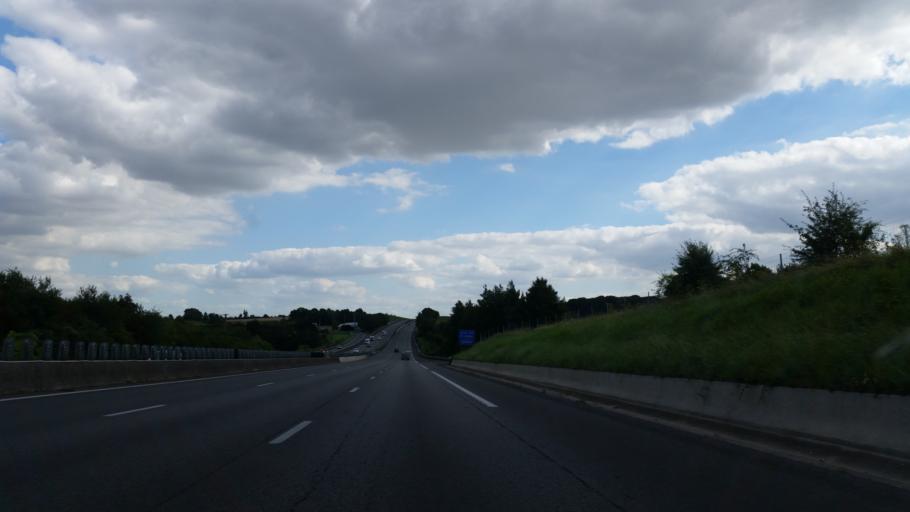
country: FR
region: Nord-Pas-de-Calais
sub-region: Departement du Pas-de-Calais
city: Croisilles
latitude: 50.1967
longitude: 2.8694
